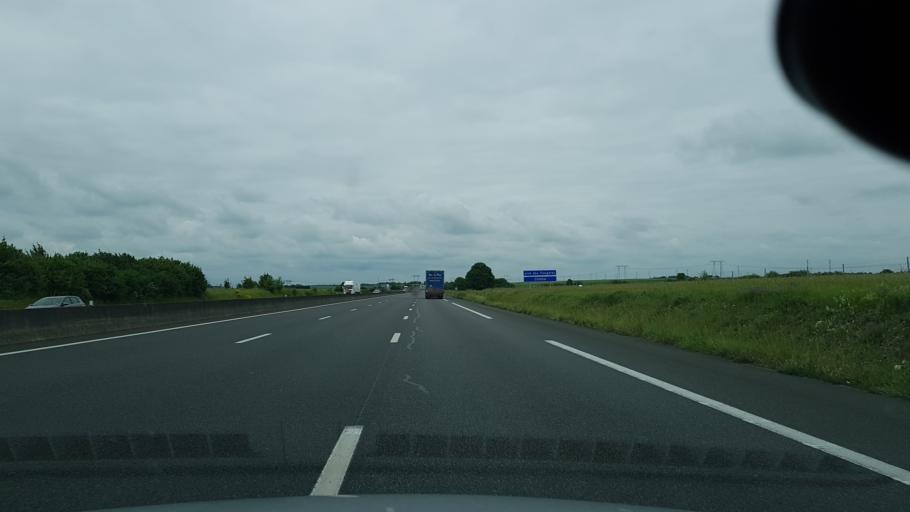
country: FR
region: Centre
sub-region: Departement du Loiret
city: Tavers
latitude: 47.7739
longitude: 1.5807
